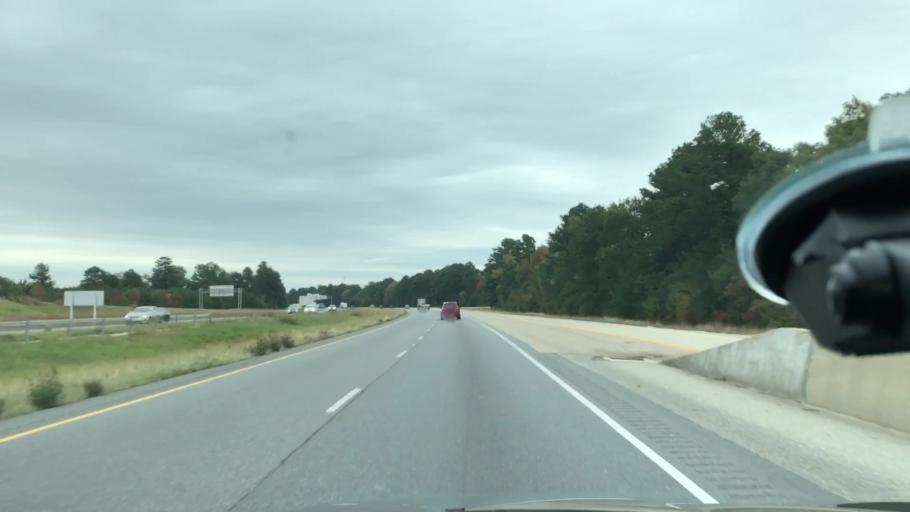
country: US
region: Arkansas
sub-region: Miller County
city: Texarkana
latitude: 33.4803
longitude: -93.9856
